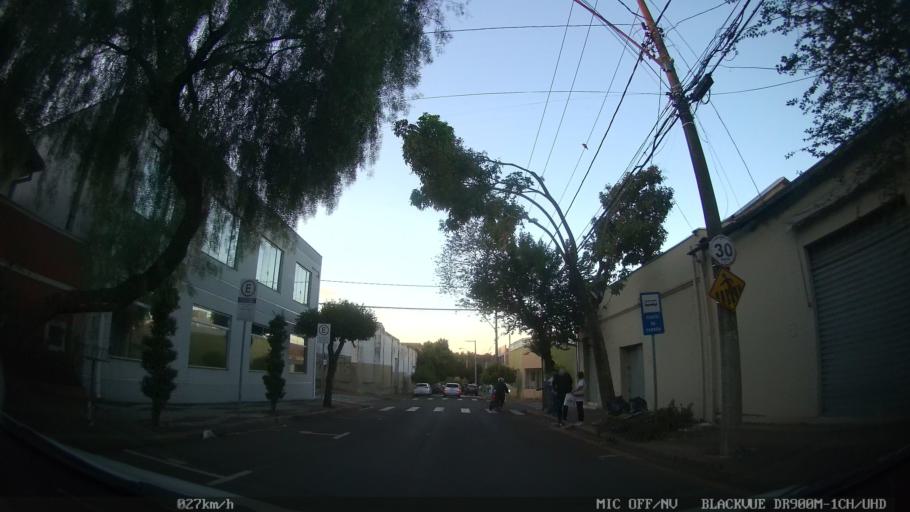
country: BR
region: Sao Paulo
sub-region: Santa Barbara D'Oeste
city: Santa Barbara d'Oeste
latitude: -22.7522
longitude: -47.4108
